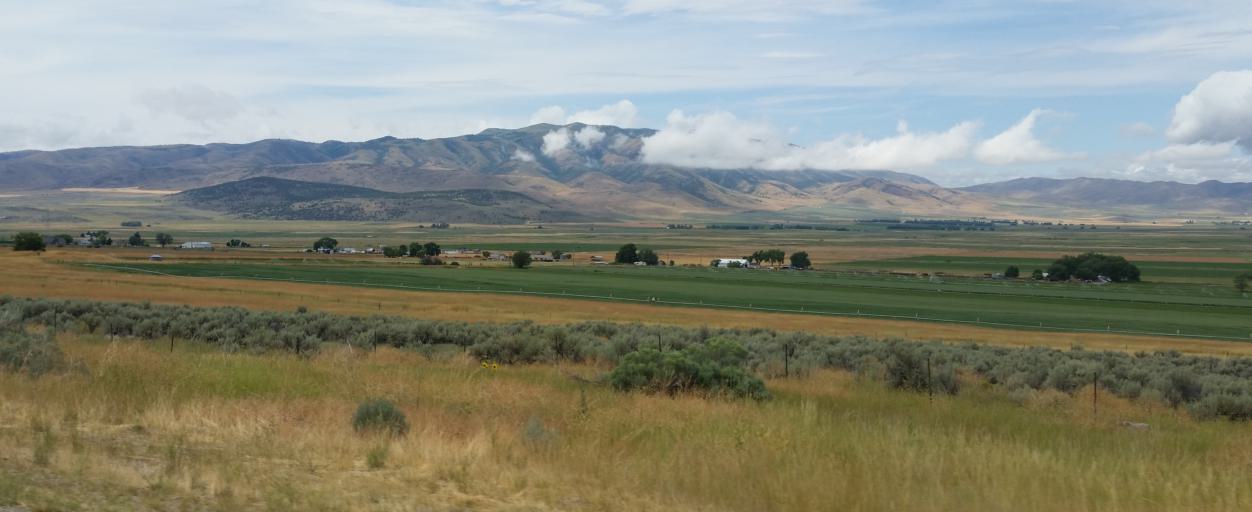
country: US
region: Idaho
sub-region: Oneida County
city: Malad City
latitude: 42.1051
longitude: -112.2172
